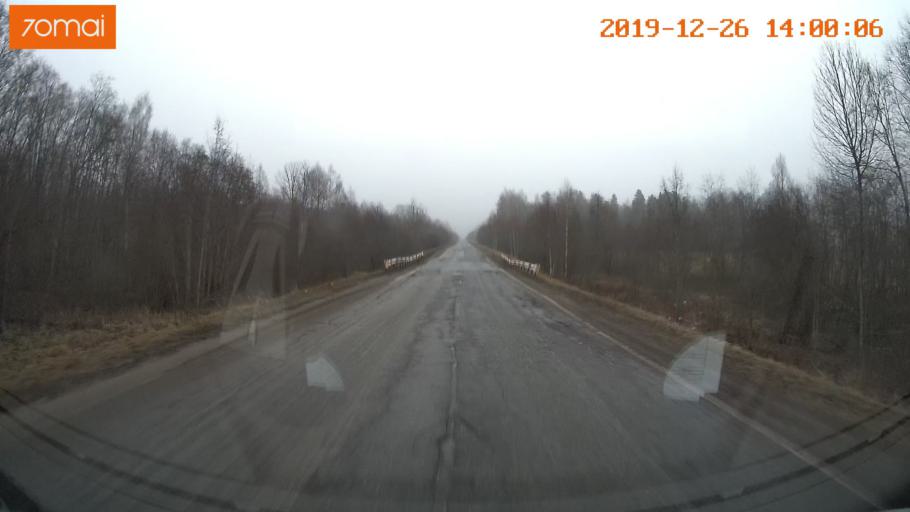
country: RU
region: Jaroslavl
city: Poshekhon'ye
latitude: 58.5605
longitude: 38.7371
